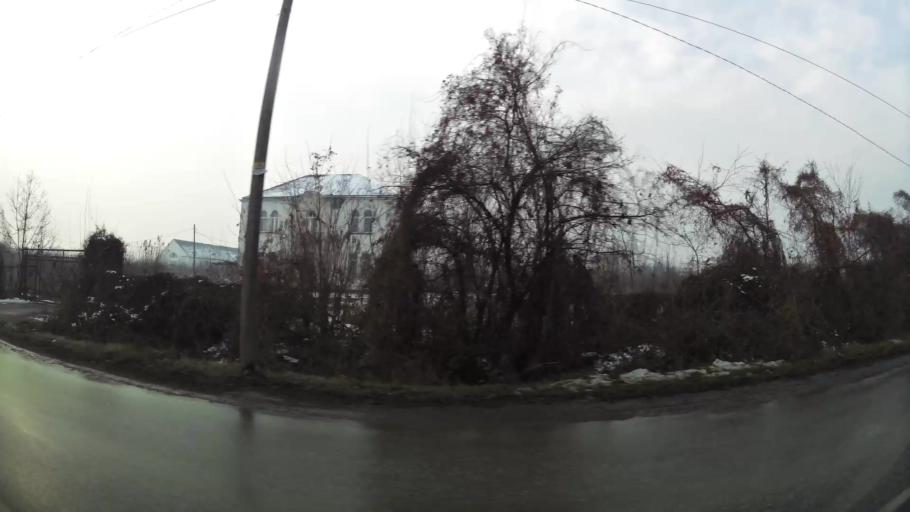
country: MK
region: Kisela Voda
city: Kisela Voda
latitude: 41.9861
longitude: 21.5185
